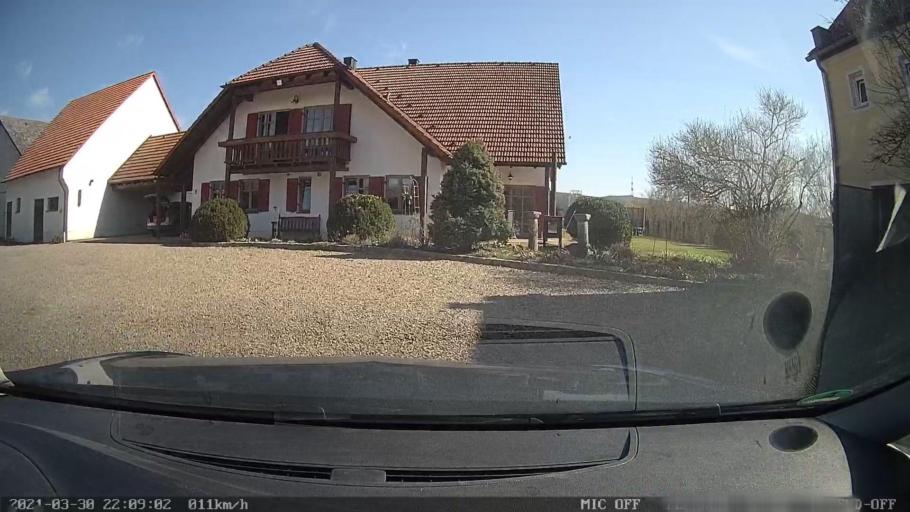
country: DE
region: Bavaria
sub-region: Upper Palatinate
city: Zeitlarn
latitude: 49.0896
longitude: 12.1254
